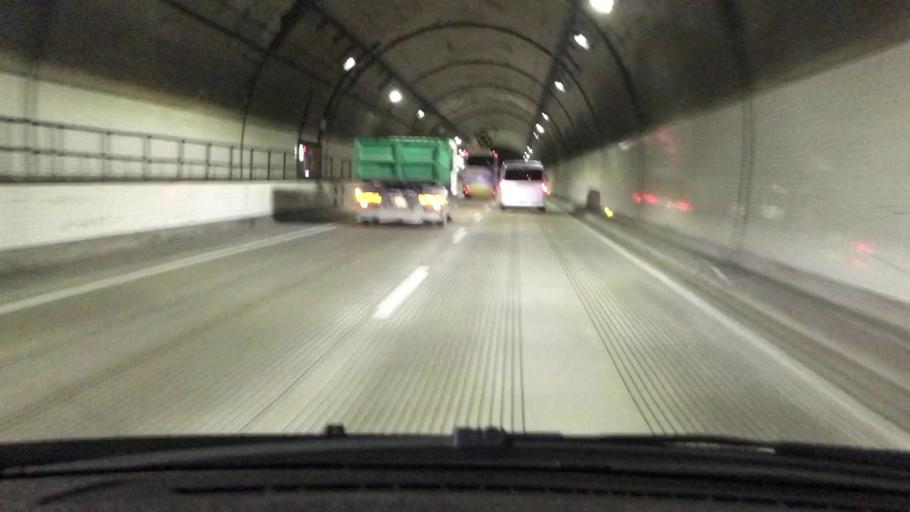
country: JP
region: Hyogo
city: Kobe
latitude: 34.7716
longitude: 135.2059
